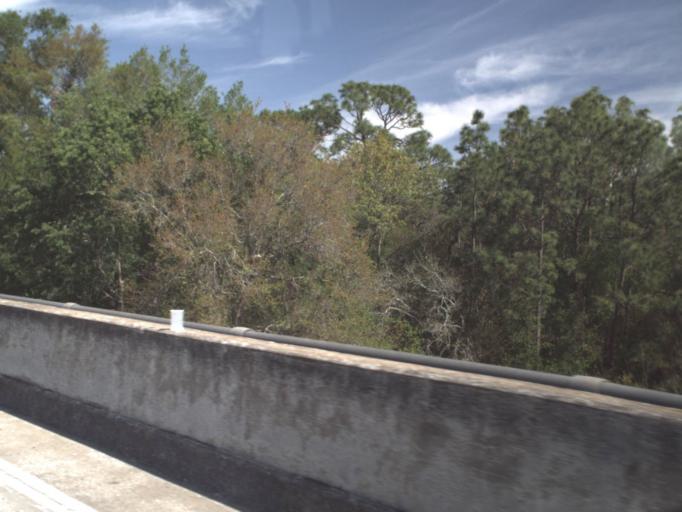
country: US
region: Florida
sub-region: Lake County
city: Lady Lake
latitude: 28.9290
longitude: -81.9264
